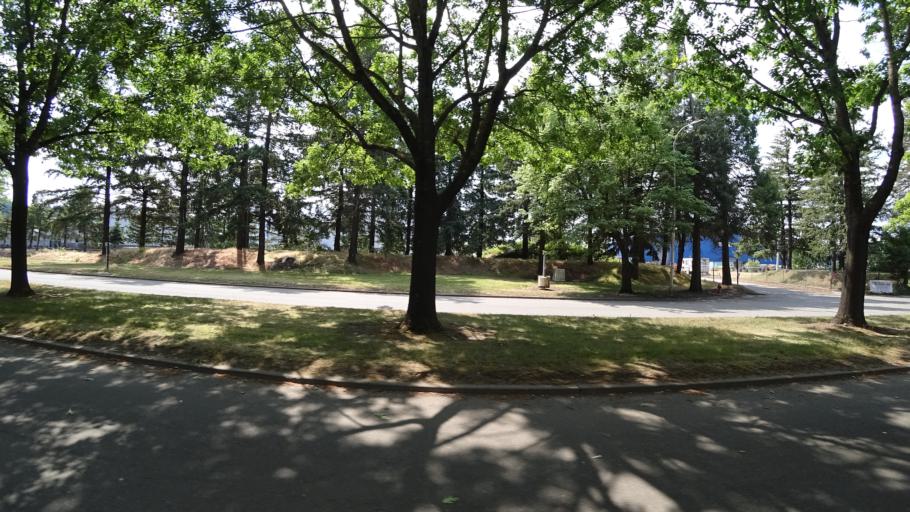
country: US
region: Oregon
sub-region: Washington County
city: Oak Hills
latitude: 45.6254
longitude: -122.7800
